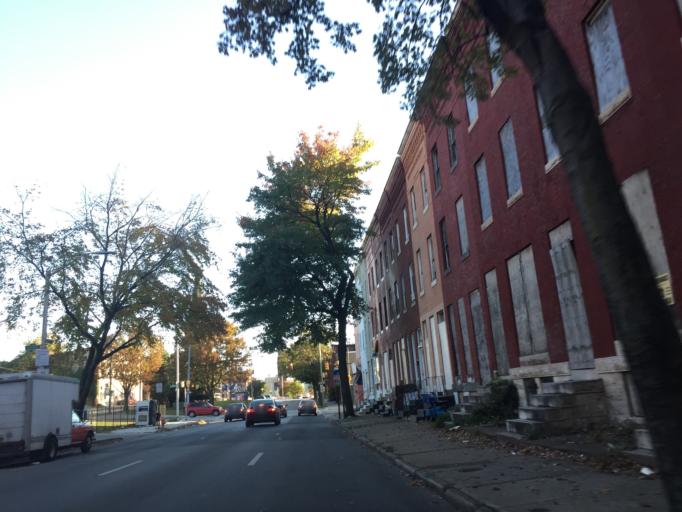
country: US
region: Maryland
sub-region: City of Baltimore
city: Baltimore
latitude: 39.3058
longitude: -76.6023
